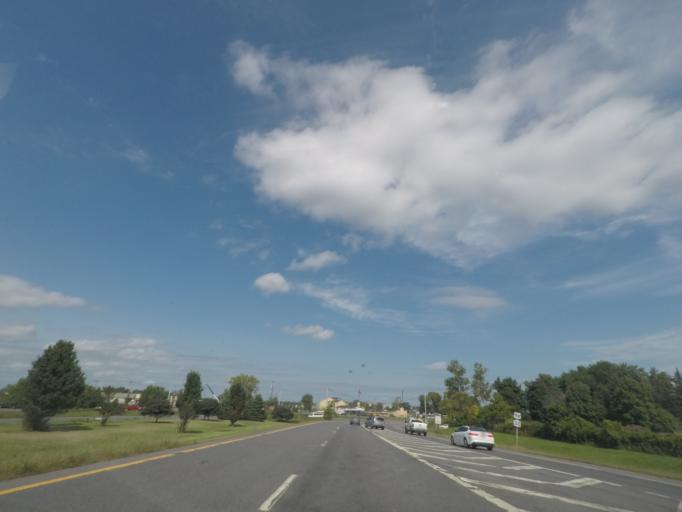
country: US
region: New York
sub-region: Albany County
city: Albany
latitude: 42.6178
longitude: -73.7844
